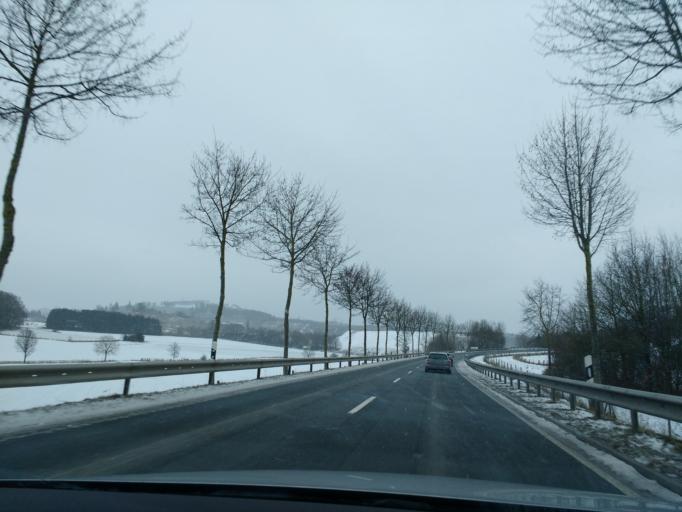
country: DE
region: North Rhine-Westphalia
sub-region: Regierungsbezirk Arnsberg
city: Brilon
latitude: 51.3923
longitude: 8.5989
